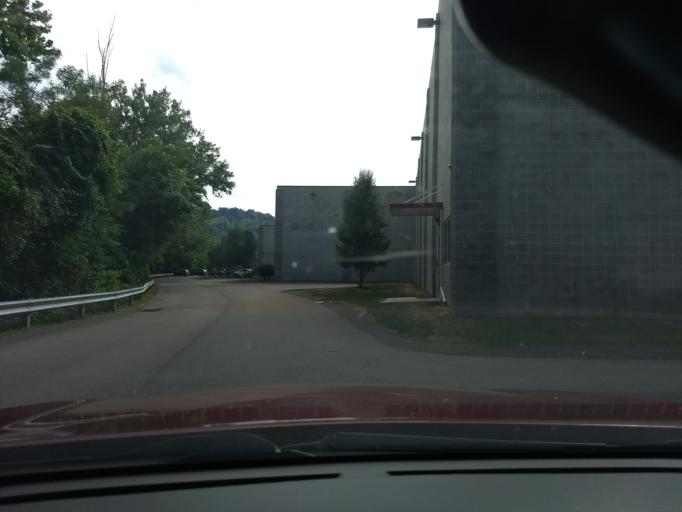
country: US
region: Pennsylvania
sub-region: Allegheny County
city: Leetsdale
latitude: 40.5571
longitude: -80.2058
